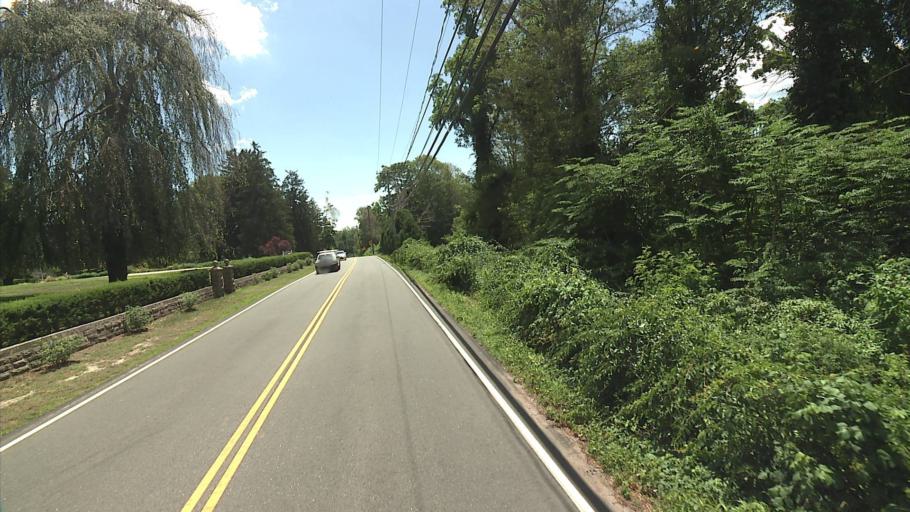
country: US
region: Connecticut
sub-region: Middlesex County
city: Moodus
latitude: 41.4856
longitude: -72.4468
